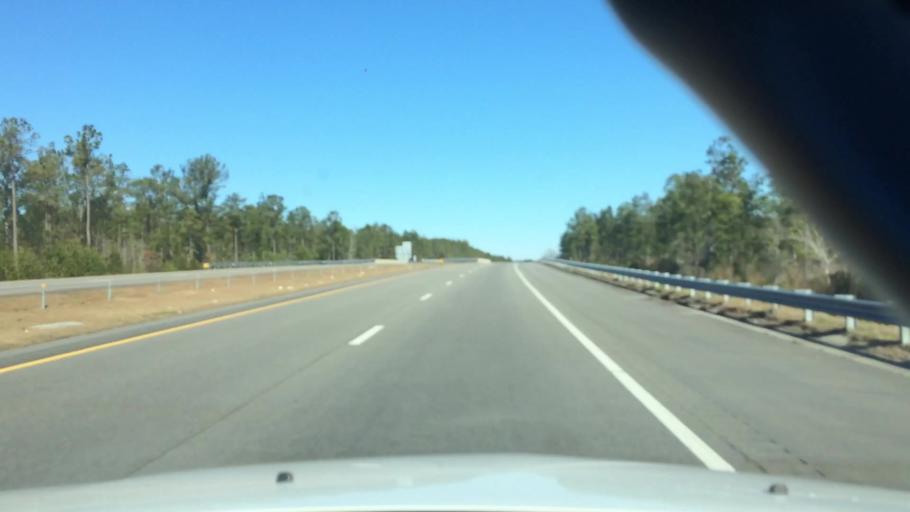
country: US
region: North Carolina
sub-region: Brunswick County
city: Leland
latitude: 34.2168
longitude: -78.0768
